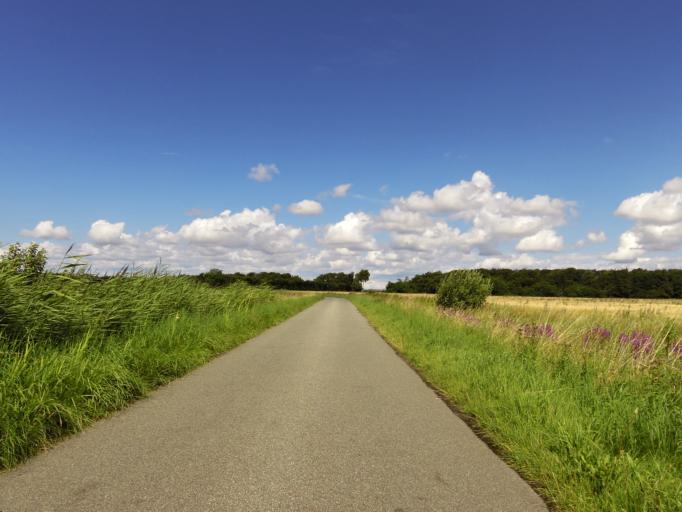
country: DK
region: South Denmark
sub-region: Esbjerg Kommune
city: Ribe
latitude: 55.3070
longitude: 8.7911
